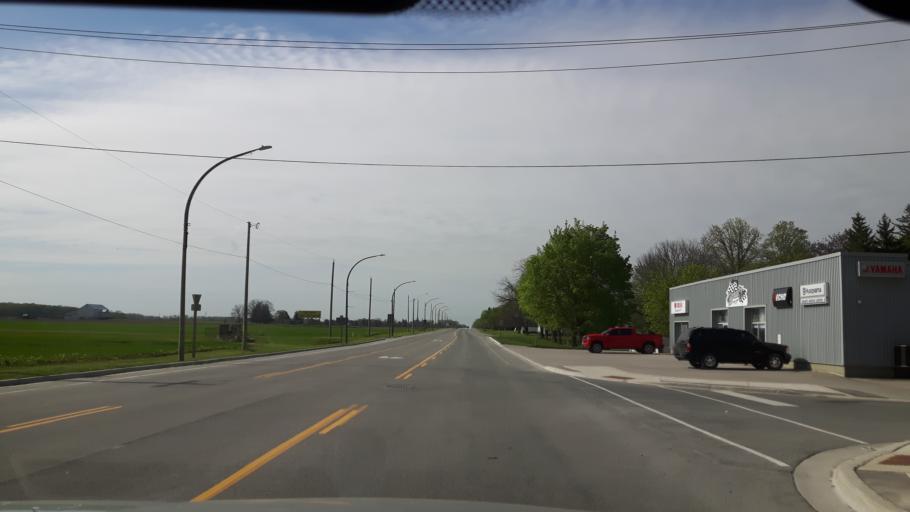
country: CA
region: Ontario
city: Bluewater
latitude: 43.4338
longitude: -81.4985
